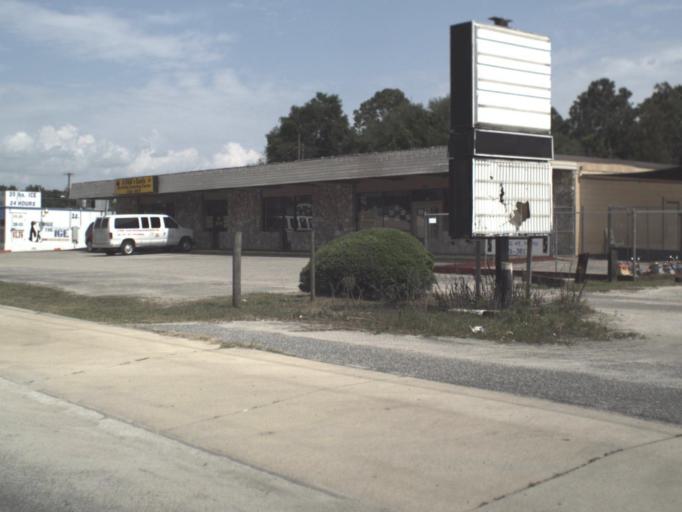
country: US
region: Florida
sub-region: Putnam County
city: Palatka
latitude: 29.6412
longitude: -81.6786
